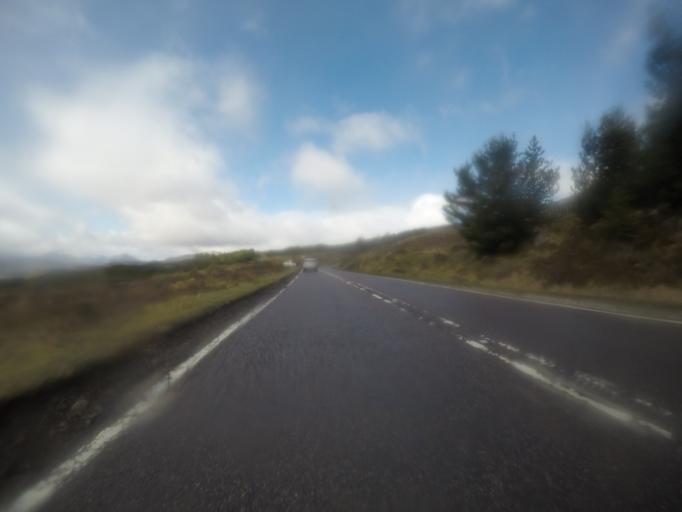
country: GB
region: Scotland
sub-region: Highland
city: Spean Bridge
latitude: 57.0865
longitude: -4.9631
